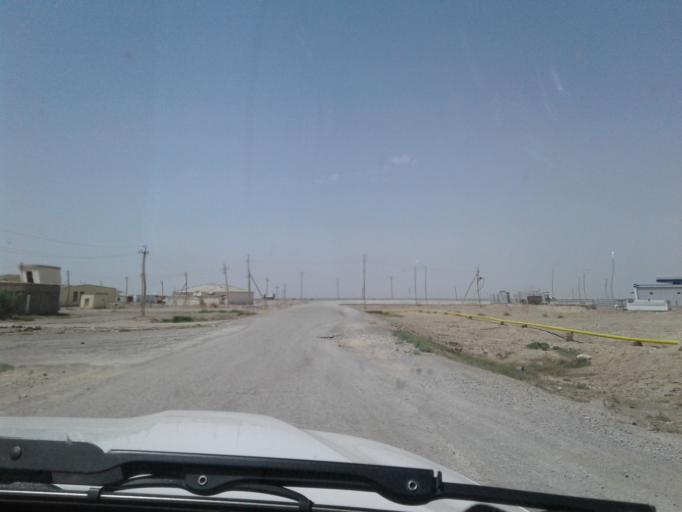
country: IR
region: Razavi Khorasan
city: Kalat-e Naderi
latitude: 37.2045
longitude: 60.0233
